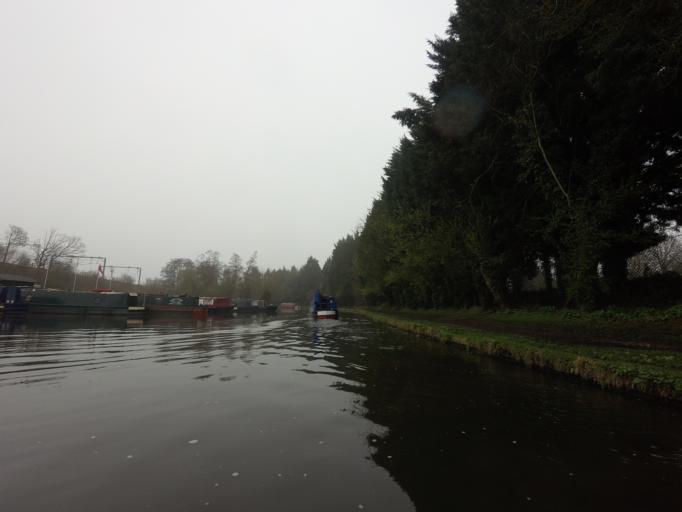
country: GB
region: England
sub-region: Hertfordshire
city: Bovingdon
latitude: 51.7462
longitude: -0.5114
